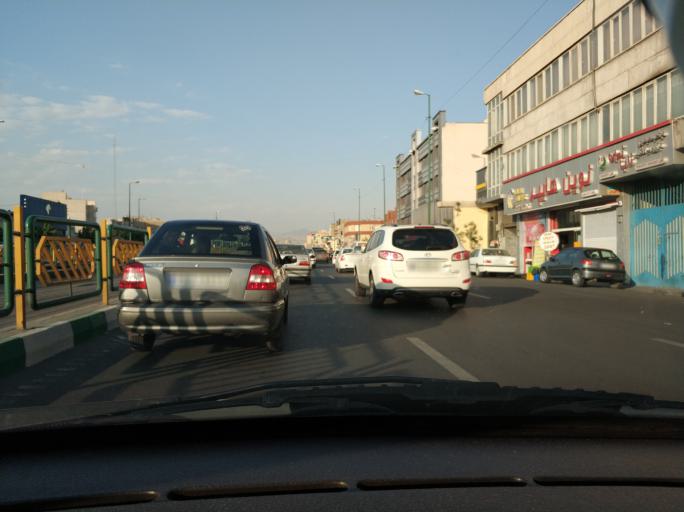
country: IR
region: Tehran
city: Tehran
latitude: 35.7085
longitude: 51.4715
